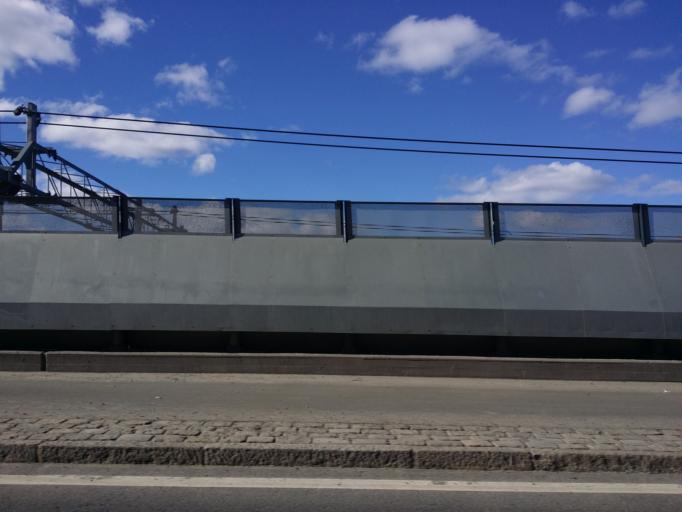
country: NO
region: Oslo
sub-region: Oslo
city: Oslo
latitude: 59.9004
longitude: 10.7582
